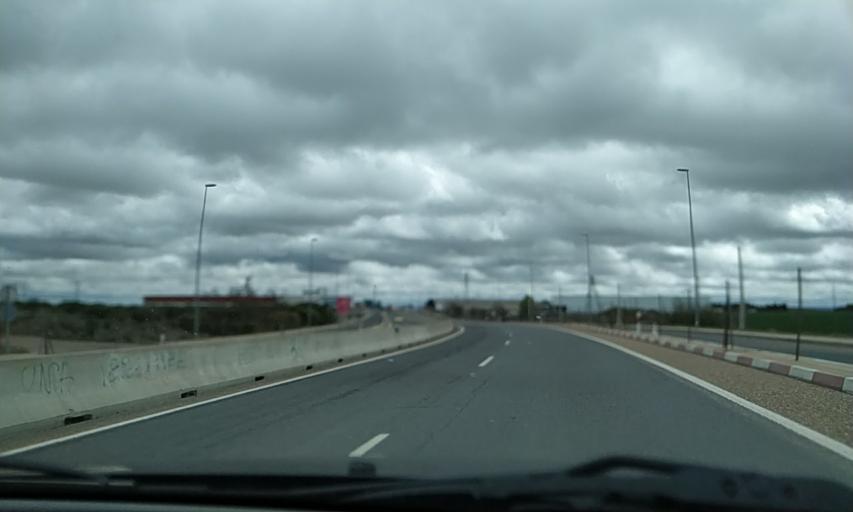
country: ES
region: Castille and Leon
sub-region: Provincia de Zamora
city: Roales
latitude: 41.5386
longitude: -5.7639
